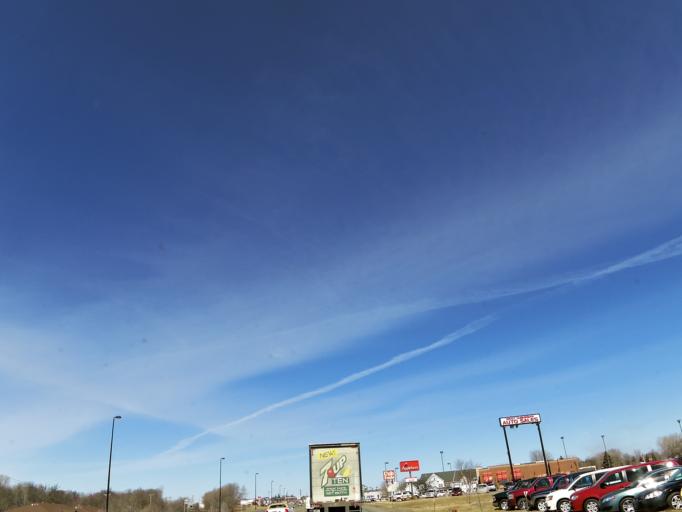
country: US
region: Minnesota
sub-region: Wright County
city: Buffalo
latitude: 45.1691
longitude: -93.8606
